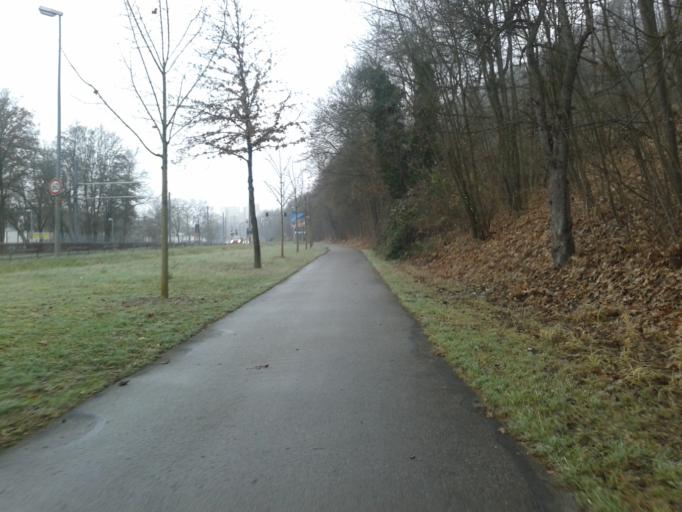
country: DE
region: Bavaria
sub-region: Swabia
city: Neu-Ulm
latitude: 48.4160
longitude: 10.0133
